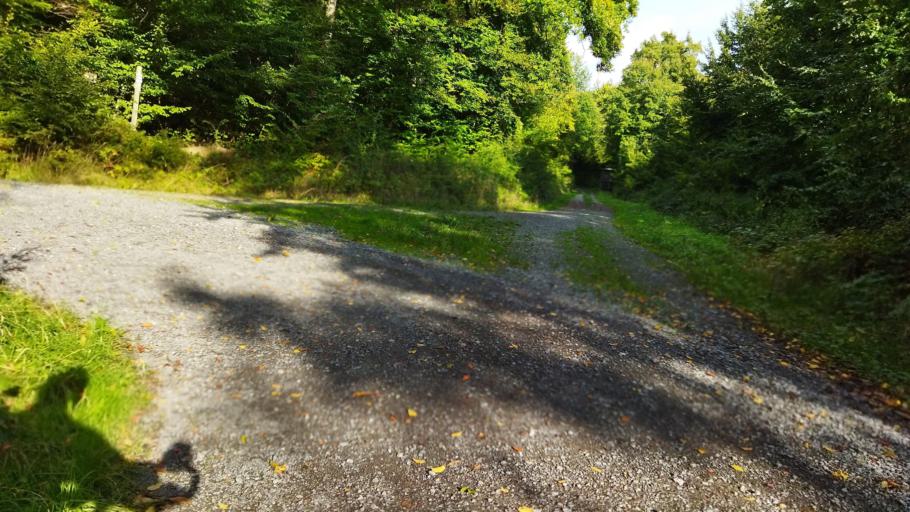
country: DE
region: Baden-Wuerttemberg
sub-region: Karlsruhe Region
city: Sternenfels
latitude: 49.0684
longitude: 8.8703
